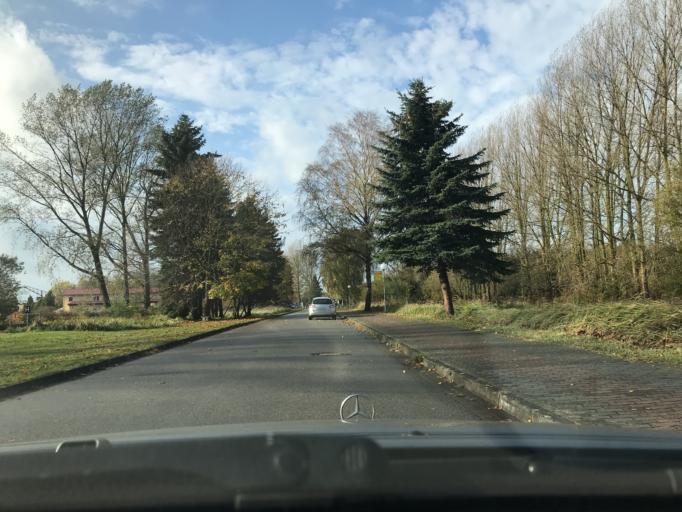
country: DE
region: Mecklenburg-Vorpommern
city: Kroslin
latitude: 54.1388
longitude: 13.7741
